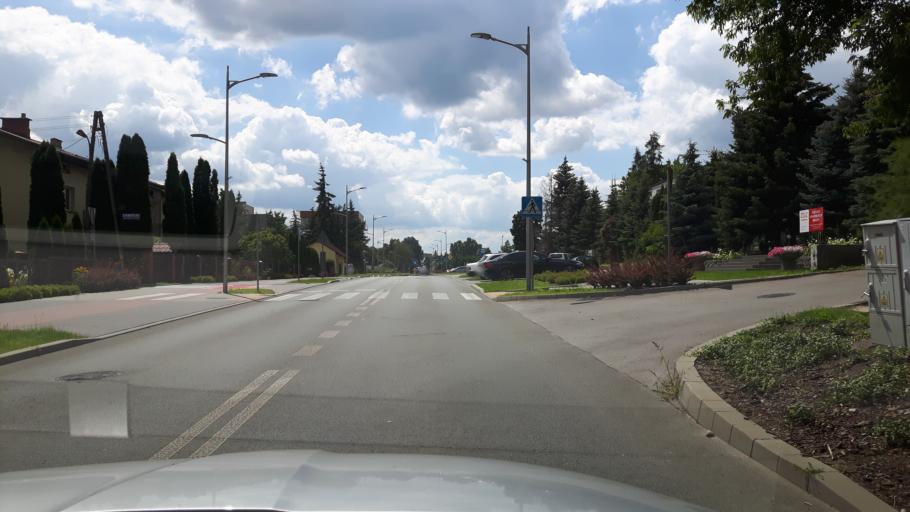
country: PL
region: Masovian Voivodeship
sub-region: Powiat wyszkowski
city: Wyszkow
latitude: 52.5877
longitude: 21.4477
